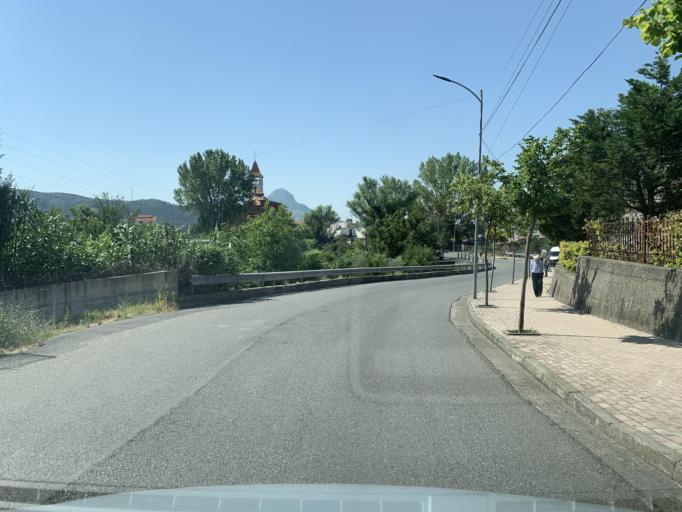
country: AL
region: Shkoder
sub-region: Rrethi i Shkodres
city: Vau i Dejes
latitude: 42.0091
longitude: 19.6401
